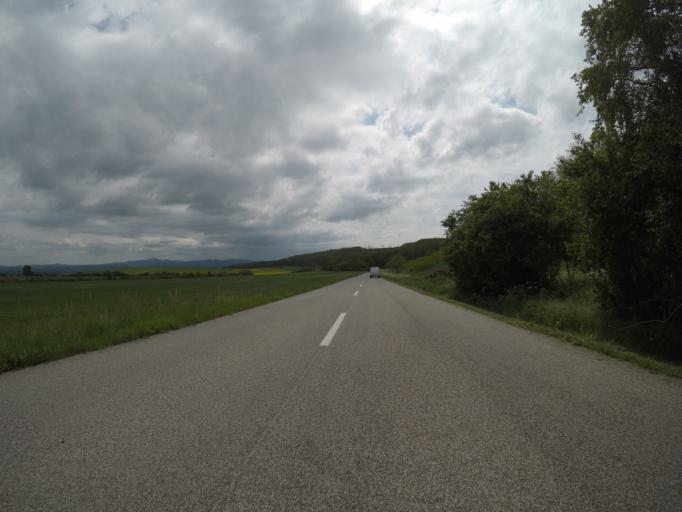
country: SK
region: Banskobystricky
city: Dudince
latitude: 48.0785
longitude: 18.7994
